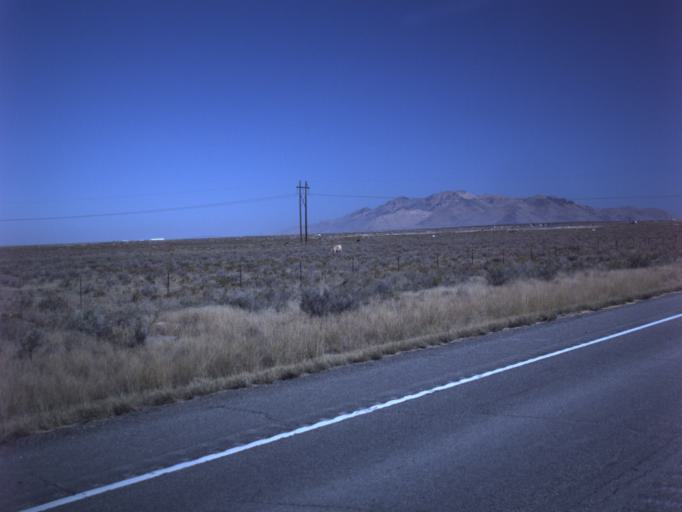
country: US
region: Utah
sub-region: Tooele County
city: Grantsville
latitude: 40.6907
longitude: -112.5369
